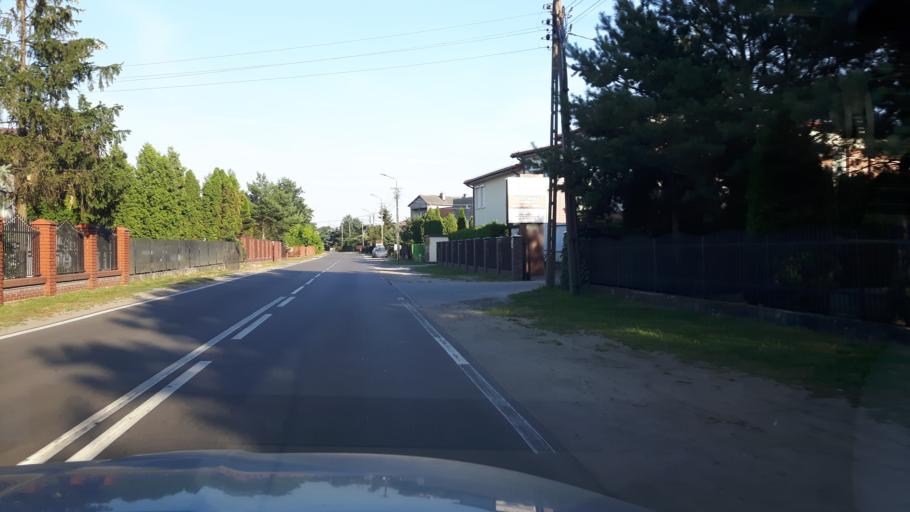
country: PL
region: Masovian Voivodeship
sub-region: Powiat wolominski
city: Slupno
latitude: 52.3641
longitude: 21.1567
